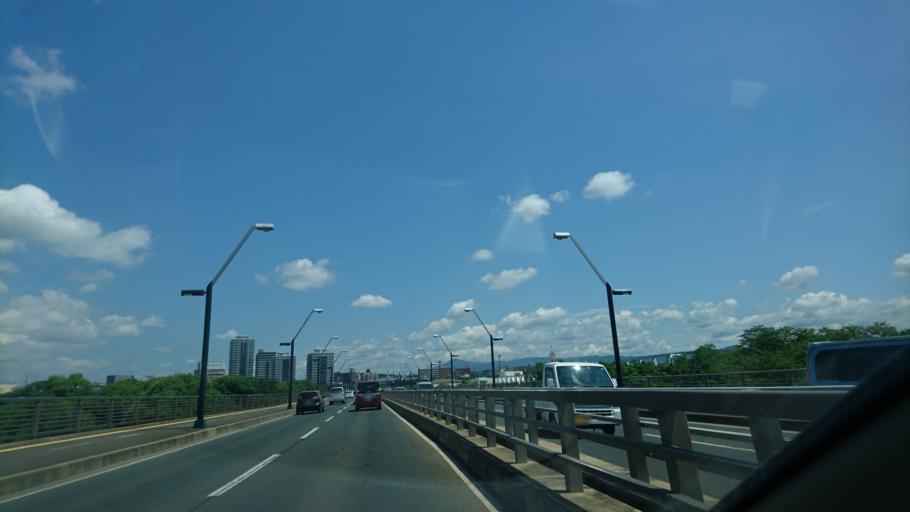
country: JP
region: Iwate
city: Morioka-shi
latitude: 39.6932
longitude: 141.1372
